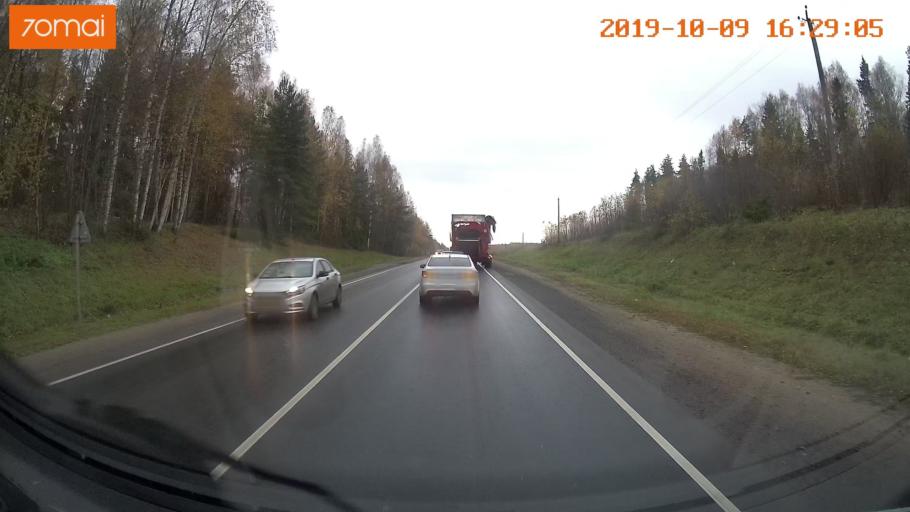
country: RU
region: Kostroma
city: Oktyabr'skiy
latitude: 57.6255
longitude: 40.9347
